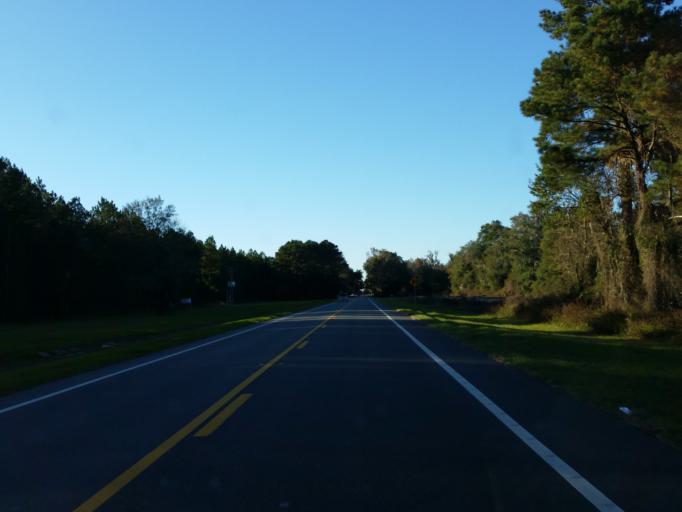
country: US
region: Florida
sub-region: Suwannee County
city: Wellborn
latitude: 30.3605
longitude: -82.7867
